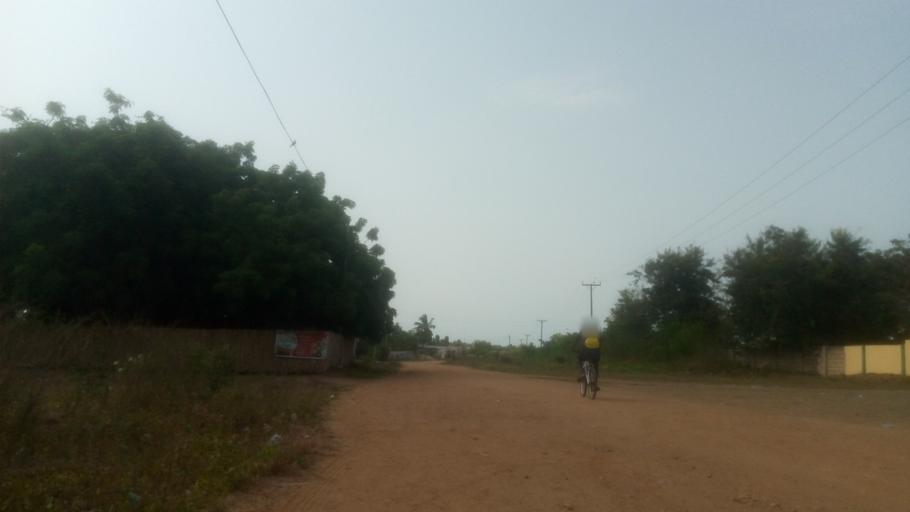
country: GH
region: Central
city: Winneba
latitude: 5.3568
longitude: -0.6362
